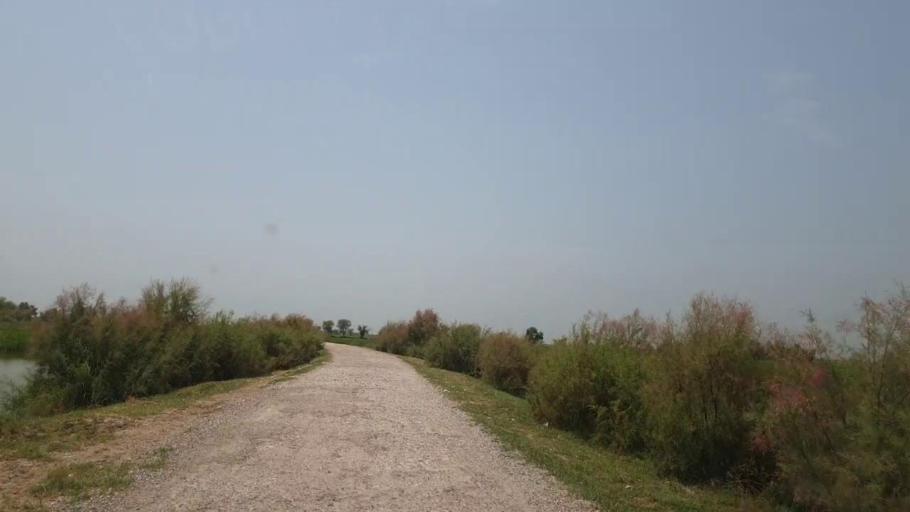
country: PK
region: Sindh
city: Shikarpur
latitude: 27.9006
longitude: 68.6323
